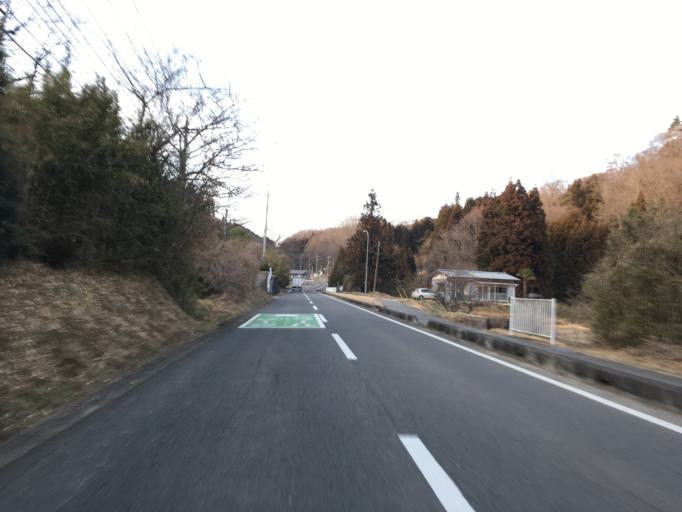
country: JP
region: Ibaraki
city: Daigo
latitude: 36.7757
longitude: 140.4272
